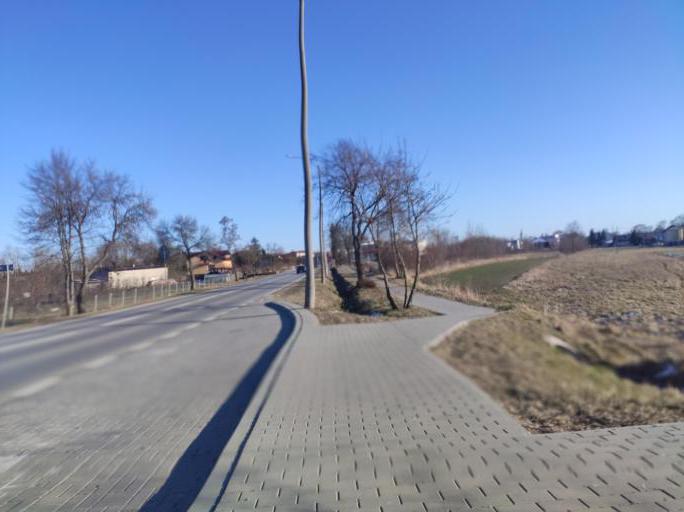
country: PL
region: Lublin Voivodeship
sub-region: Powiat lubartowski
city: Kock
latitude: 51.6450
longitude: 22.4443
